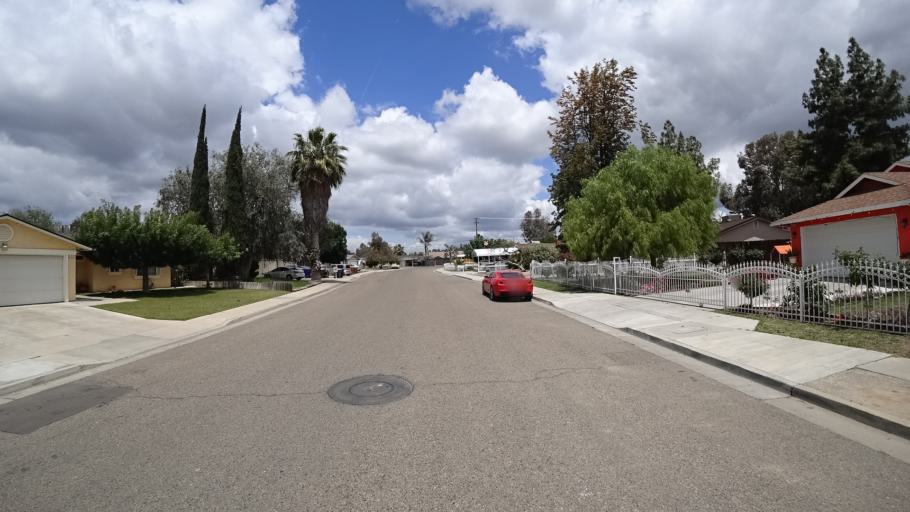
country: US
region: California
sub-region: Kings County
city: Hanford
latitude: 36.3359
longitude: -119.6329
